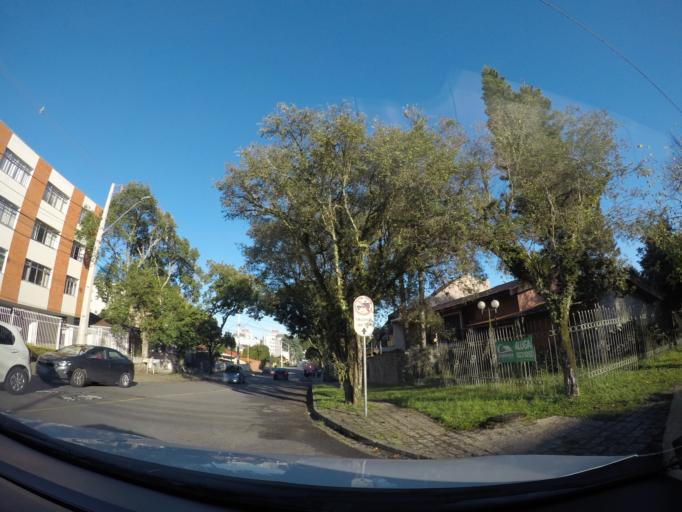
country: BR
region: Parana
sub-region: Curitiba
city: Curitiba
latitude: -25.4072
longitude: -49.2670
